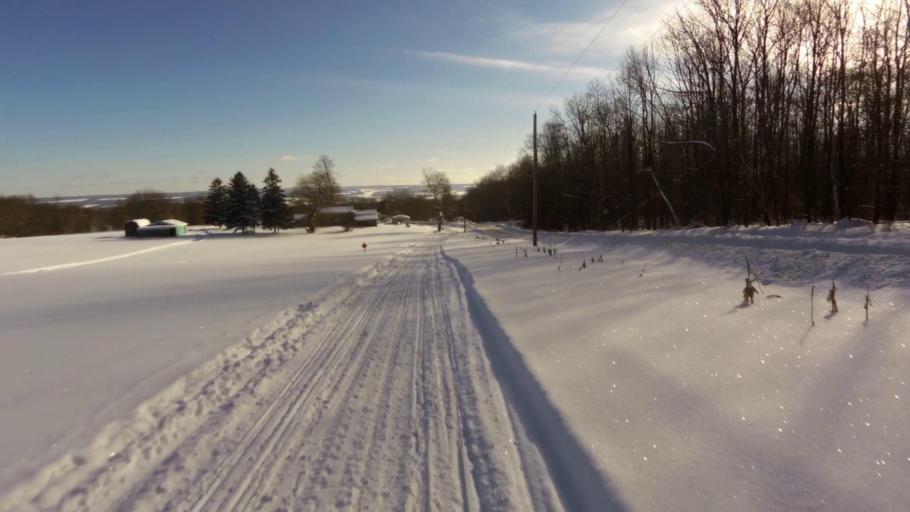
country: US
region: New York
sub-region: Chautauqua County
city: Falconer
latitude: 42.2606
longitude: -79.1149
